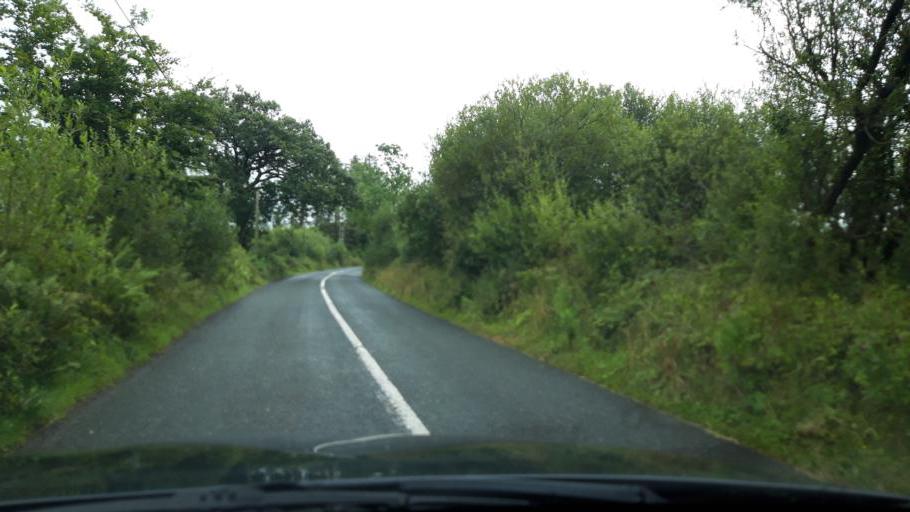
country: IE
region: Munster
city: Cahir
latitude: 52.1686
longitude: -7.8562
